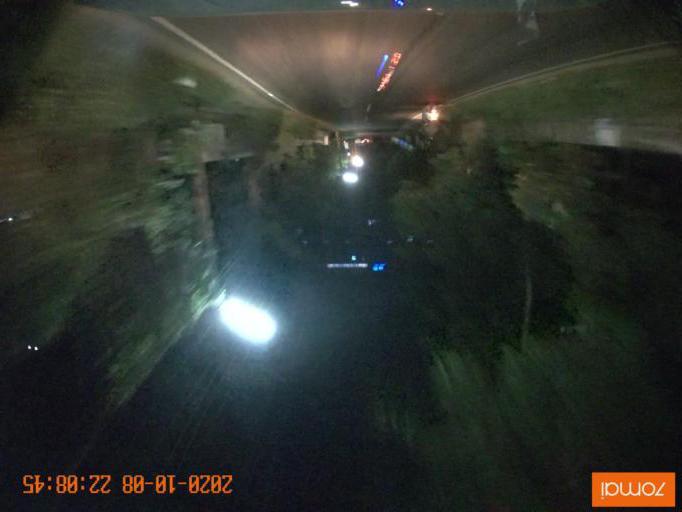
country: IN
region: Kerala
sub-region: Malappuram
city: Tirur
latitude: 10.8789
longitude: 75.9314
